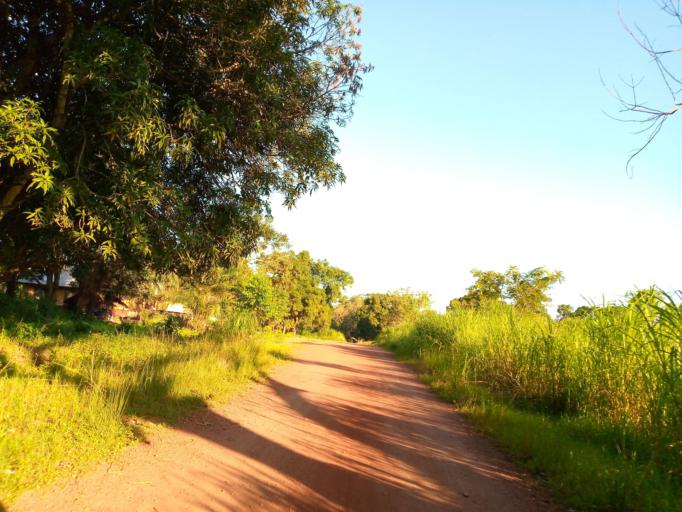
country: SL
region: Northern Province
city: Yonibana
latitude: 8.4511
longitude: -12.2443
